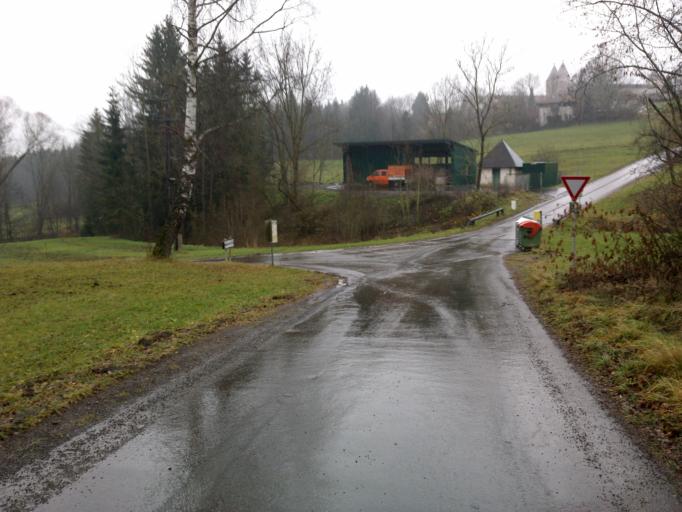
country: AT
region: Styria
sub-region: Politischer Bezirk Murtal
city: Seckau
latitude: 47.2786
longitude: 14.7895
